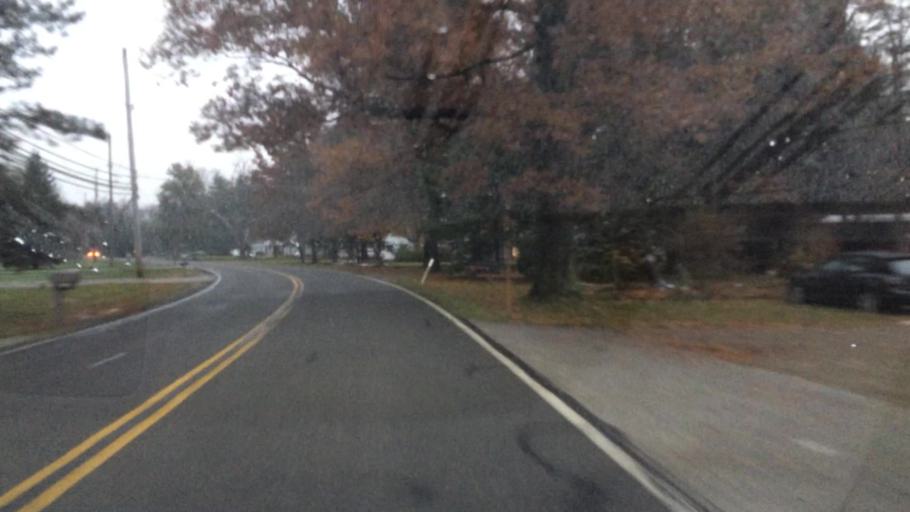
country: US
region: Ohio
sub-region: Cuyahoga County
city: Olmsted Falls
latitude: 41.3536
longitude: -81.9257
